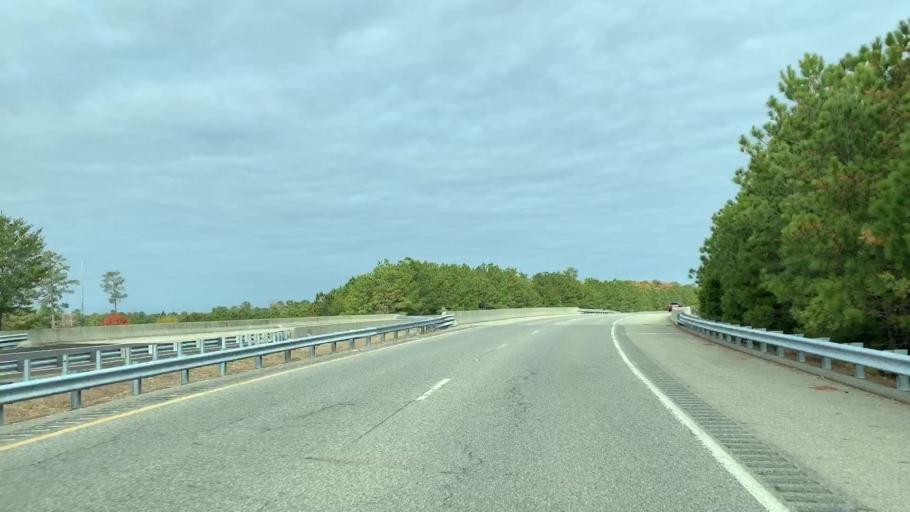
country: US
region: Virginia
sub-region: James City County
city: Williamsburg
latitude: 37.2727
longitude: -76.7517
